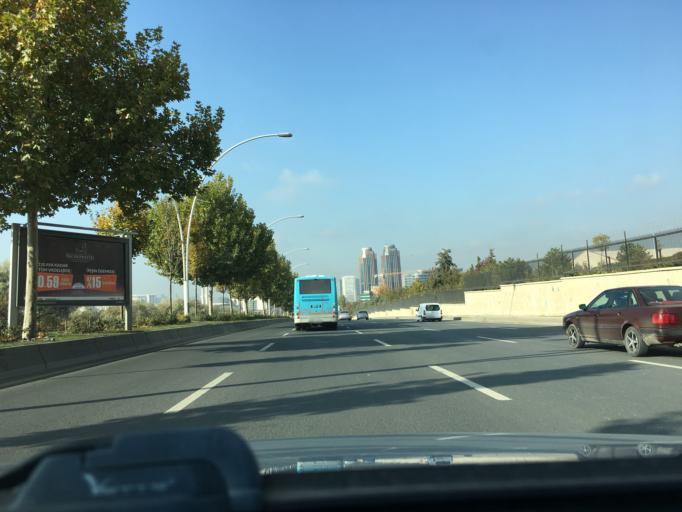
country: TR
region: Ankara
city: Batikent
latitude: 39.9083
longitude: 32.7741
